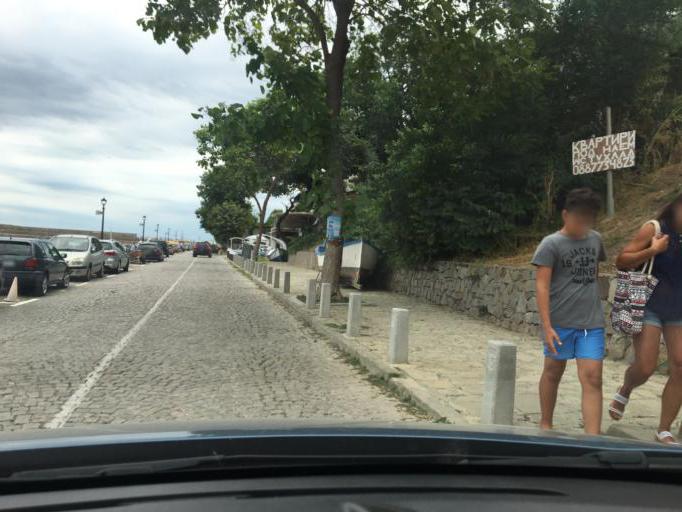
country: BG
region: Burgas
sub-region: Obshtina Sozopol
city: Sozopol
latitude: 42.4222
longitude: 27.6922
